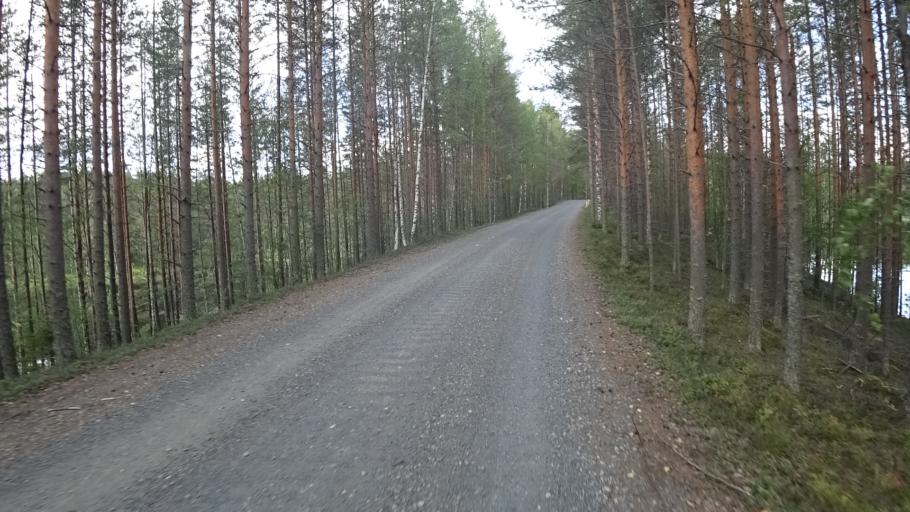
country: FI
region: North Karelia
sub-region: Joensuu
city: Ilomantsi
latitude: 62.6193
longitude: 31.1949
